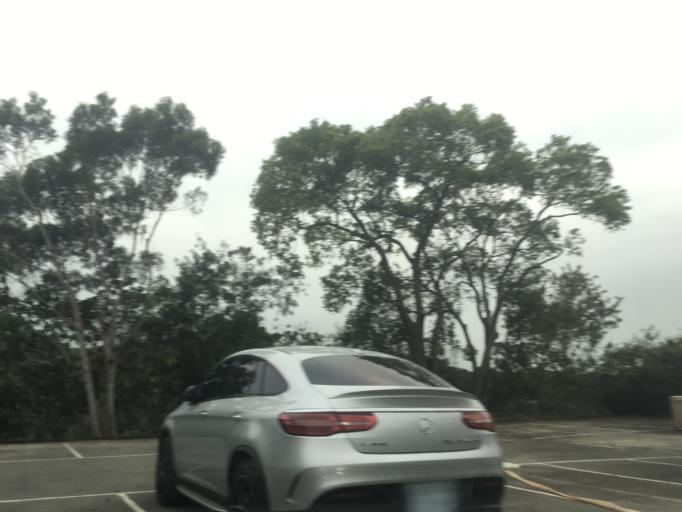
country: TW
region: Taiwan
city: Zhongxing New Village
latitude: 24.0336
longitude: 120.7473
